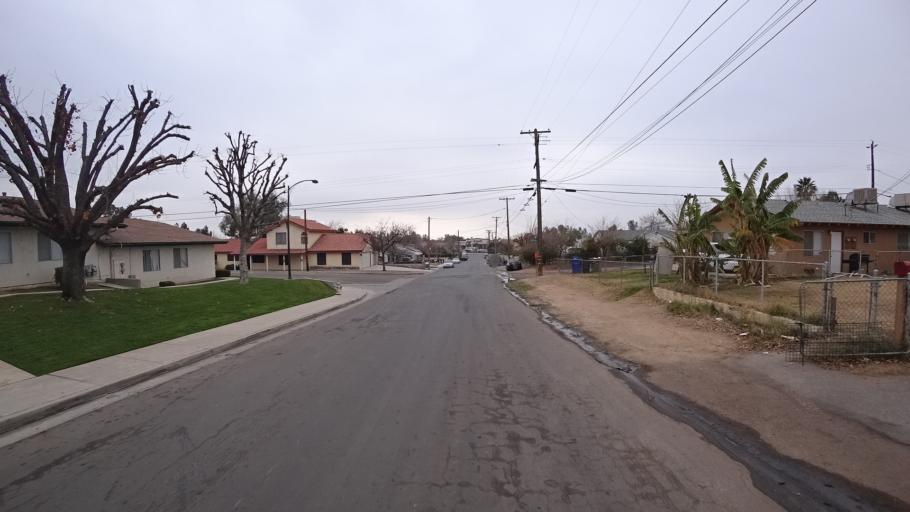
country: US
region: California
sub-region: Kern County
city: Bakersfield
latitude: 35.3781
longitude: -118.9378
